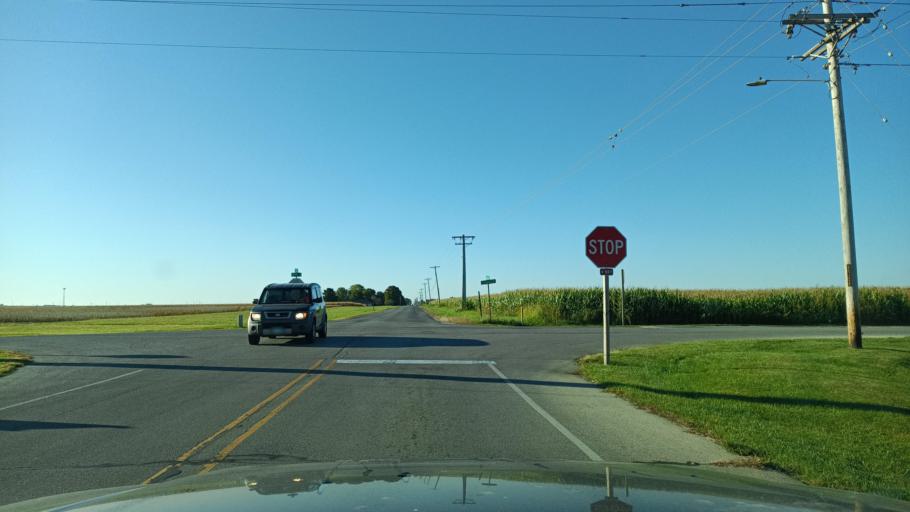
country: US
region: Illinois
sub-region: Champaign County
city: Savoy
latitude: 40.0547
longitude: -88.2383
